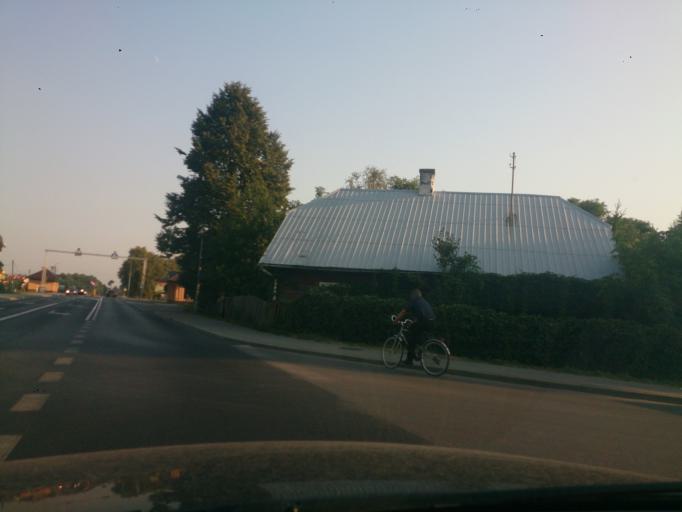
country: PL
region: Subcarpathian Voivodeship
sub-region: Powiat kolbuszowski
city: Cmolas
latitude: 50.2951
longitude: 21.7446
